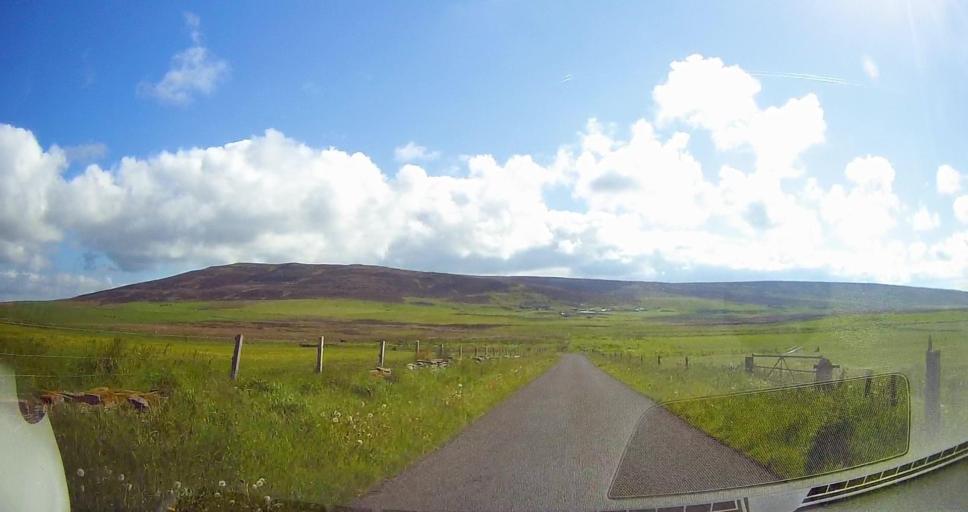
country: GB
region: Scotland
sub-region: Orkney Islands
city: Stromness
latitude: 58.9863
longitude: -3.1467
